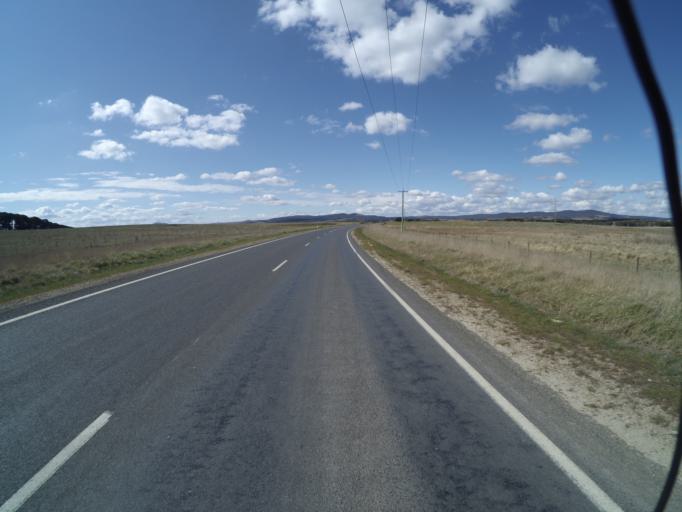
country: AU
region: New South Wales
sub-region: Palerang
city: Bungendore
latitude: -35.2164
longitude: 149.4660
